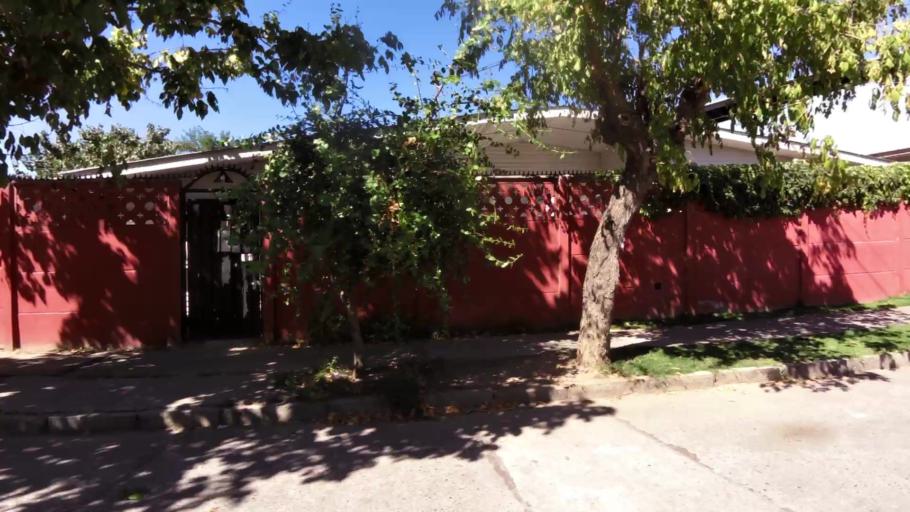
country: CL
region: O'Higgins
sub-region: Provincia de Cachapoal
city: Rancagua
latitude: -34.1773
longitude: -70.7364
